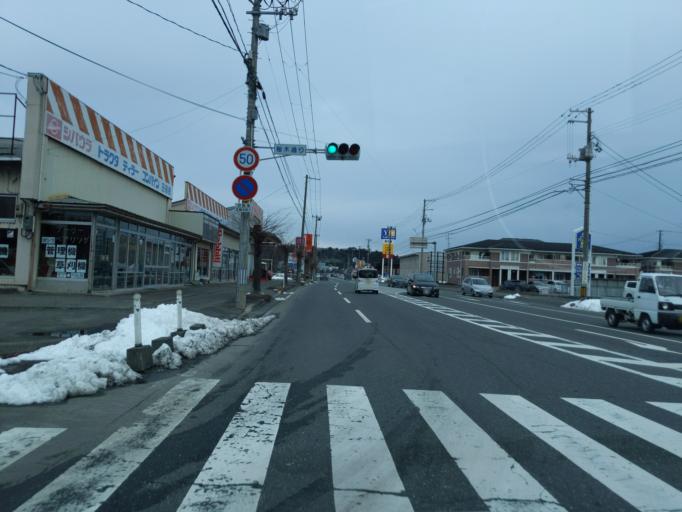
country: JP
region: Iwate
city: Mizusawa
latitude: 39.1839
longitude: 141.1720
